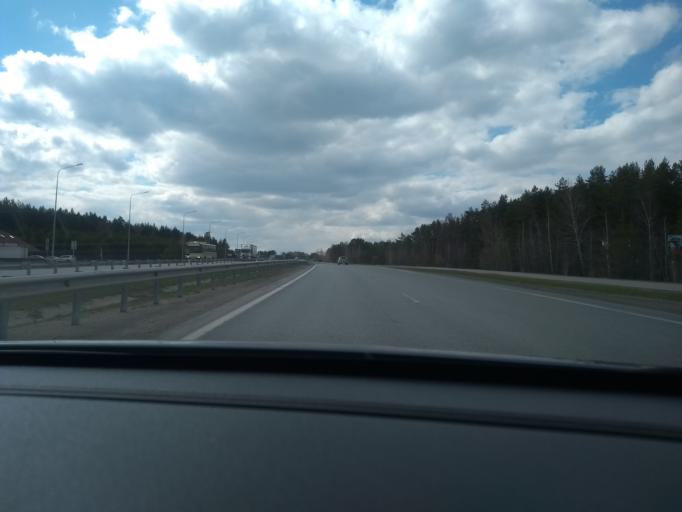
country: RU
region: Tatarstan
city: Yelabuga
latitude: 55.7814
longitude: 52.1910
